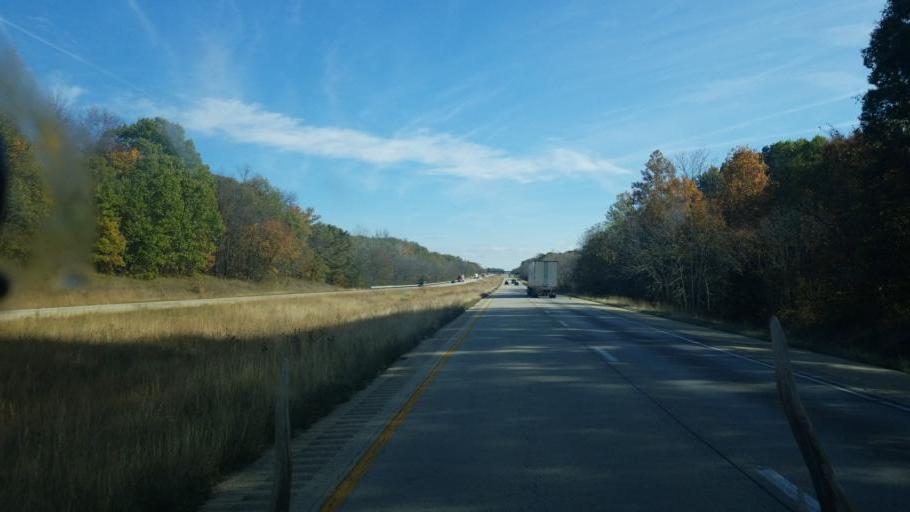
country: US
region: Illinois
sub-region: Effingham County
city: Altamont
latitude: 39.0691
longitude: -88.6649
